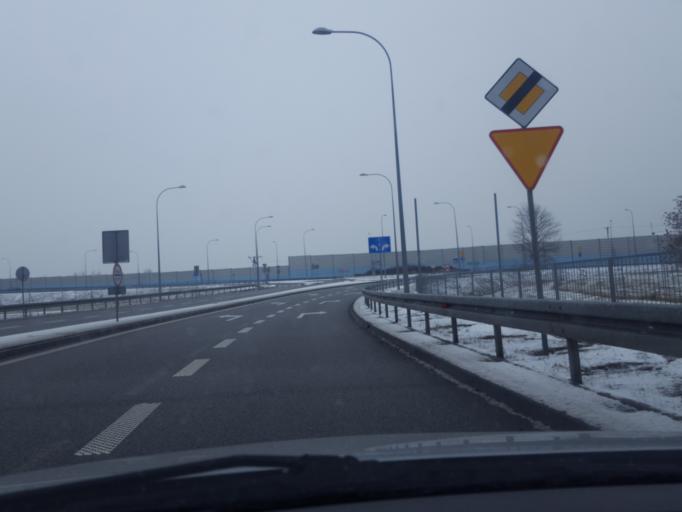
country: PL
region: Lodz Voivodeship
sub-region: powiat Lowicki
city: Lyszkowice
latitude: 51.9890
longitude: 19.9037
